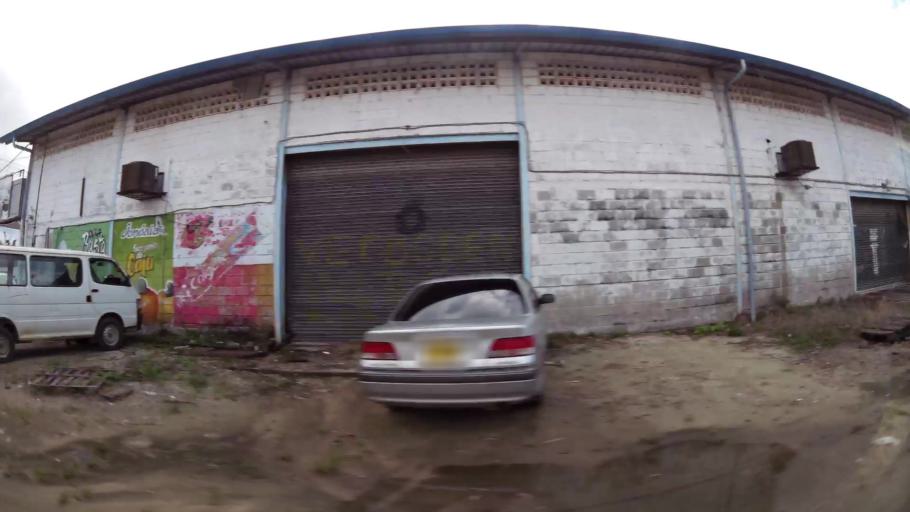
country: SR
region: Paramaribo
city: Paramaribo
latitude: 5.8468
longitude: -55.2320
